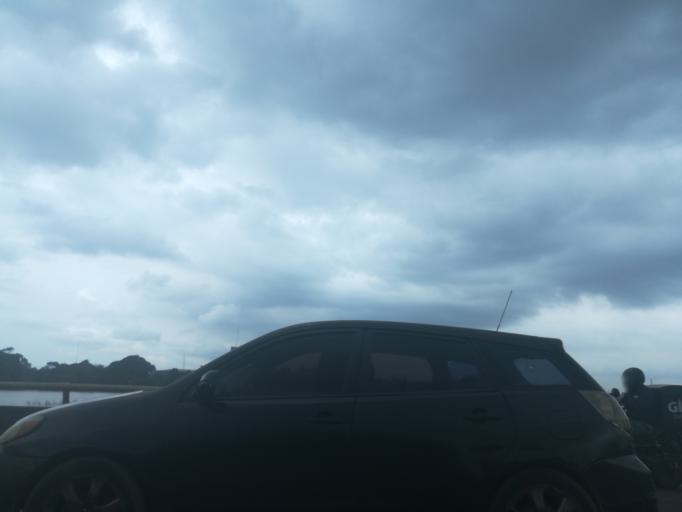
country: NG
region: Lagos
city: Makoko
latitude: 6.5220
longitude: 3.4047
